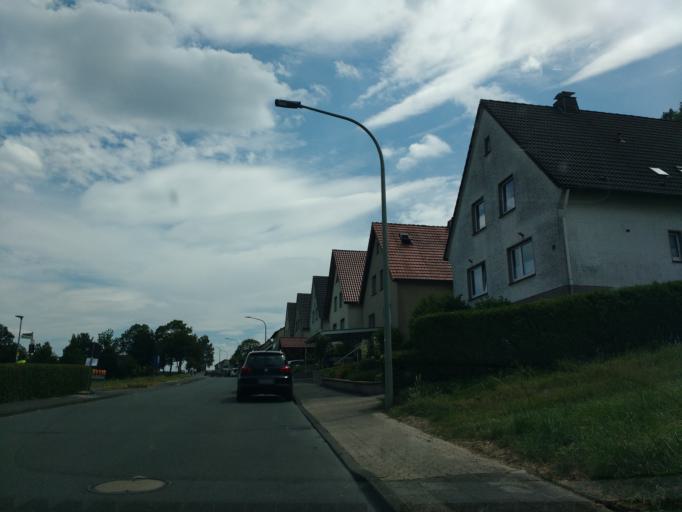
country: DE
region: North Rhine-Westphalia
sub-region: Regierungsbezirk Detmold
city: Altenbeken
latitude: 51.7607
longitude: 8.9391
